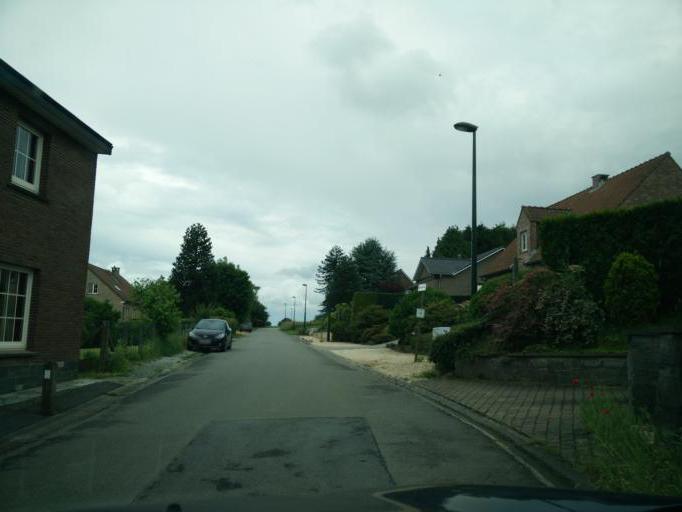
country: BE
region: Flanders
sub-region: Provincie Vlaams-Brabant
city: Beersel
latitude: 50.7233
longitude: 4.2956
